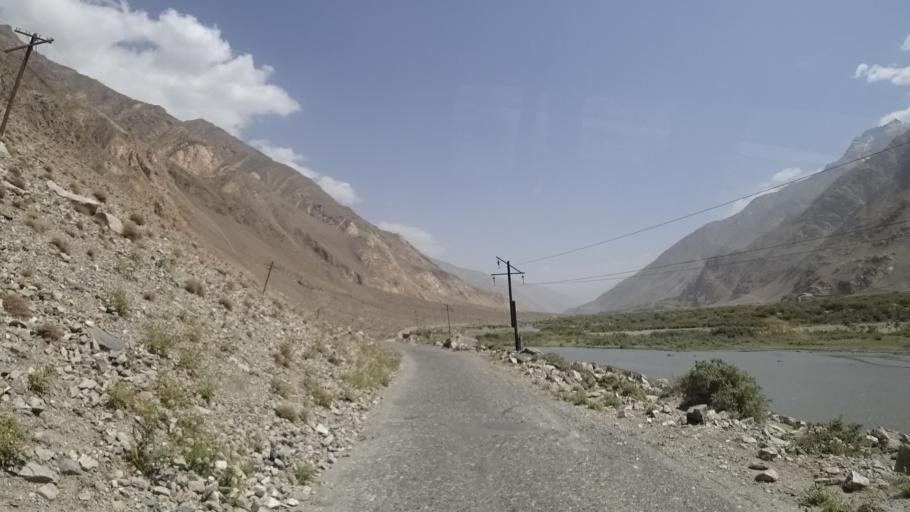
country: TJ
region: Gorno-Badakhshan
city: Ishqoshim
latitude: 36.9554
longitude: 71.4713
